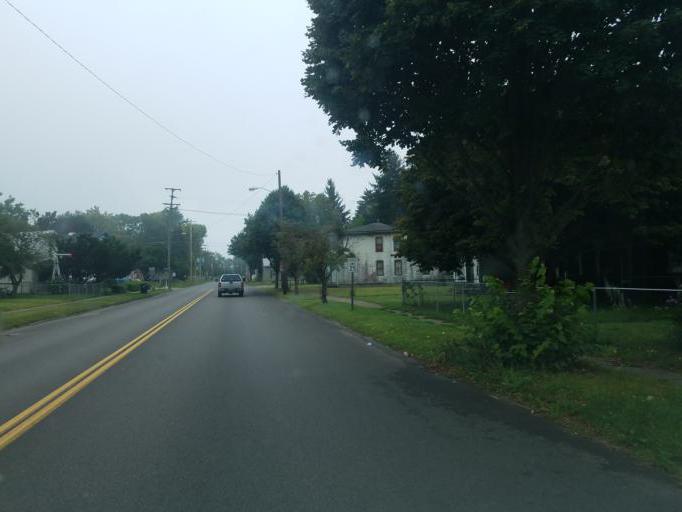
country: US
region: Ohio
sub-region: Knox County
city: Mount Vernon
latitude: 40.3994
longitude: -82.4900
